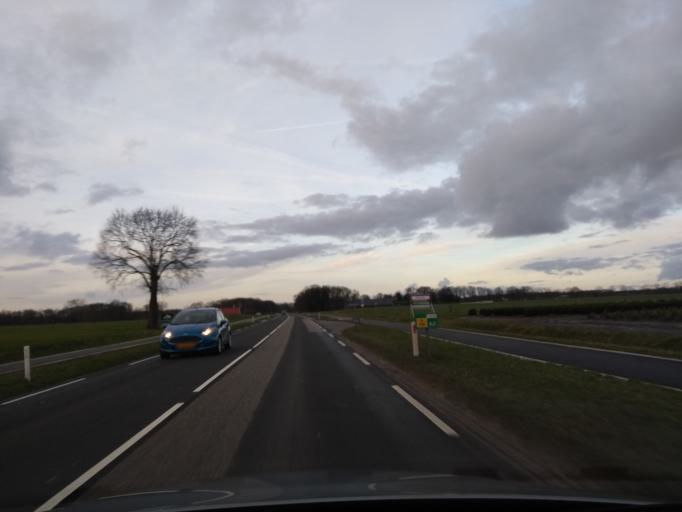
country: NL
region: Overijssel
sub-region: Gemeente Oldenzaal
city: Oldenzaal
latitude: 52.3148
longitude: 6.8600
